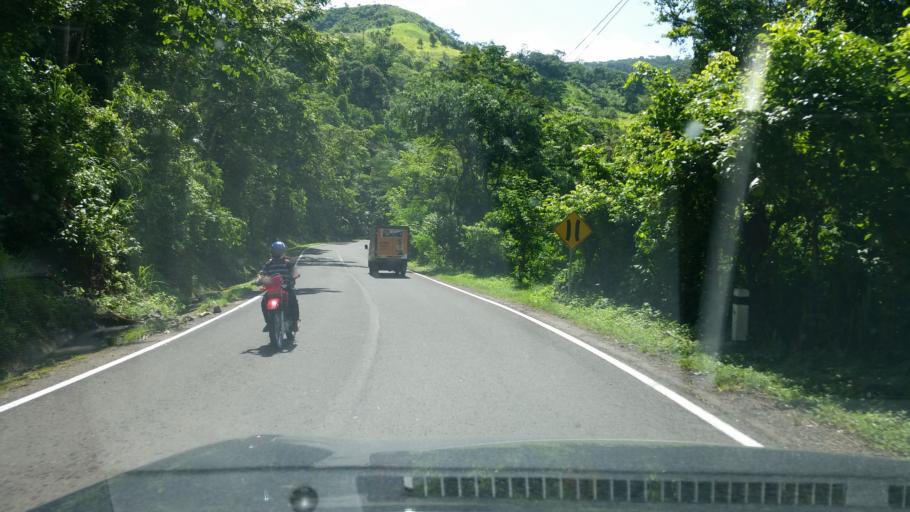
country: NI
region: Matagalpa
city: San Ramon
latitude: 13.0011
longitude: -85.8107
